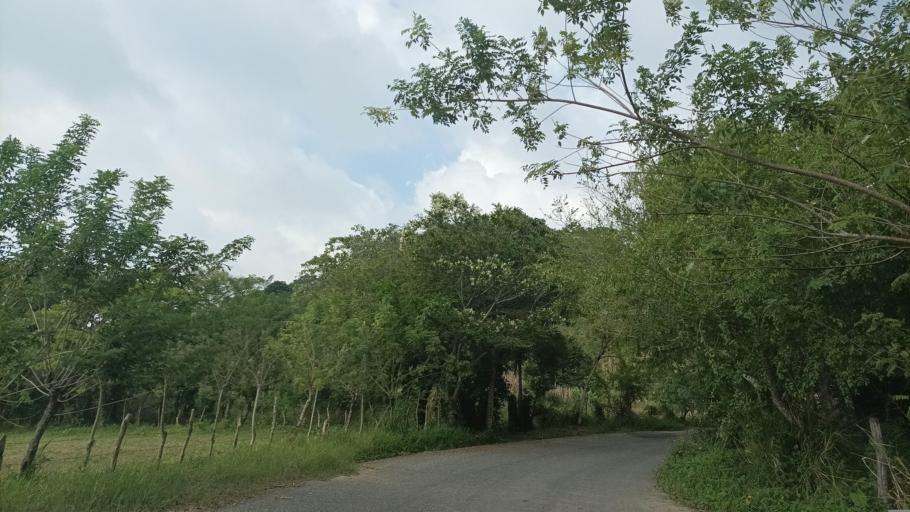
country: MX
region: Veracruz
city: Allende
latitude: 18.1176
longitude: -94.2910
